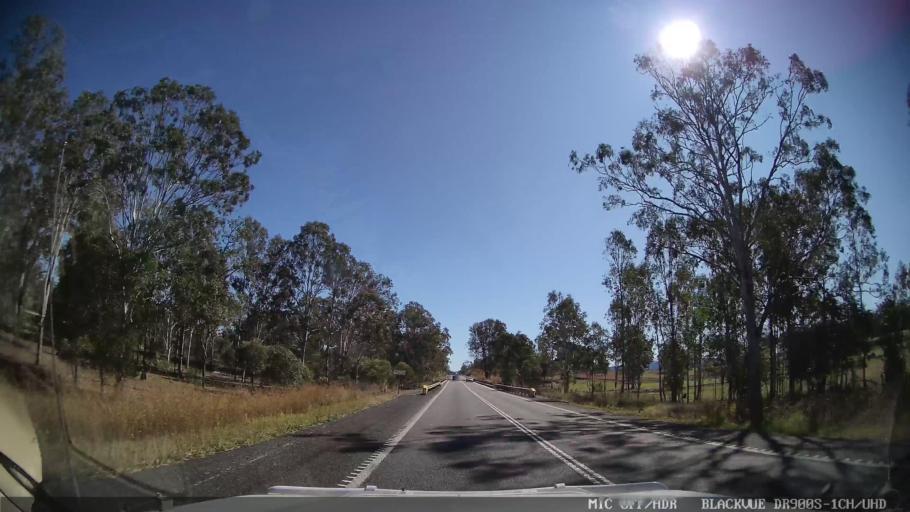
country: AU
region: Queensland
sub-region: Gympie Regional Council
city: Gympie
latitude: -26.0403
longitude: 152.5705
